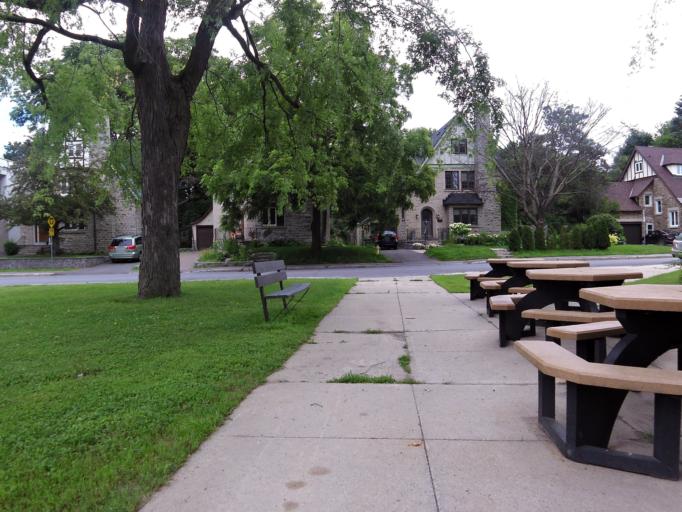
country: CA
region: Ontario
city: Ottawa
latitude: 45.3935
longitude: -75.7195
